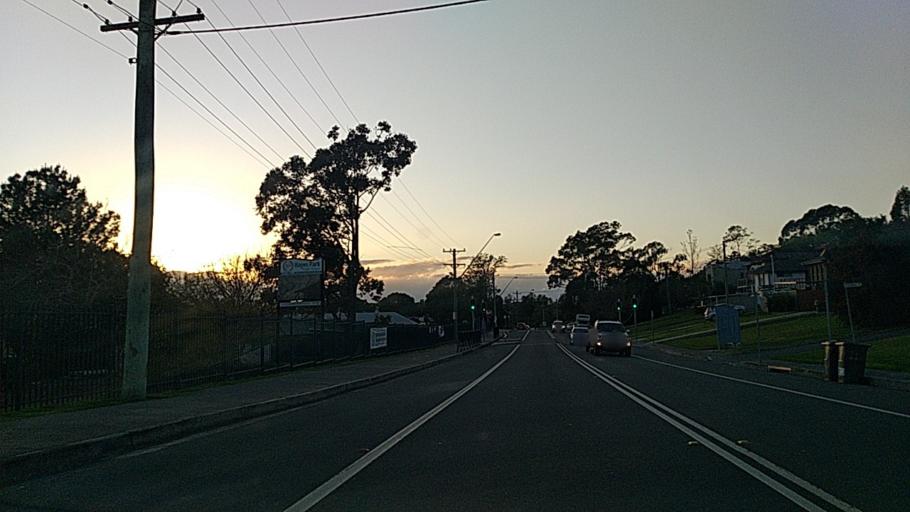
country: AU
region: New South Wales
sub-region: Wollongong
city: Koonawarra
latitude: -34.4922
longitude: 150.8150
